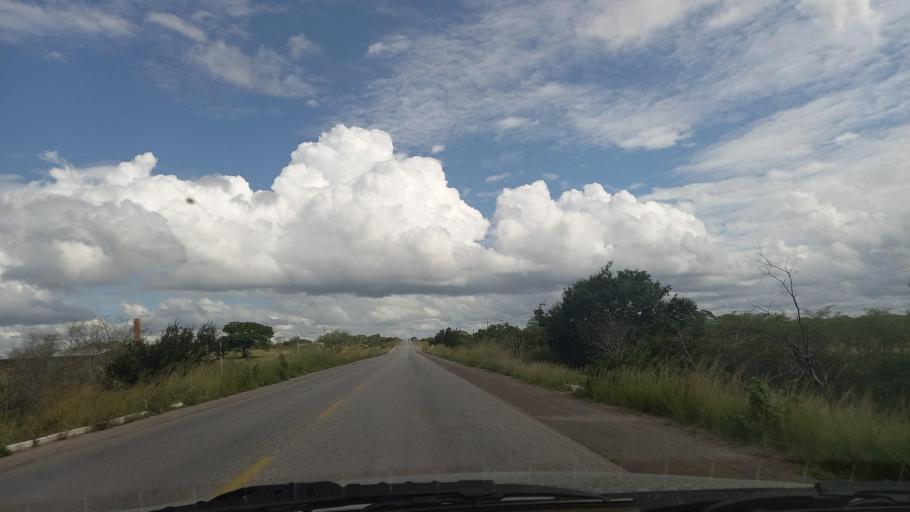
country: BR
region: Pernambuco
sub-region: Cachoeirinha
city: Cachoeirinha
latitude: -8.4537
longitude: -36.2125
